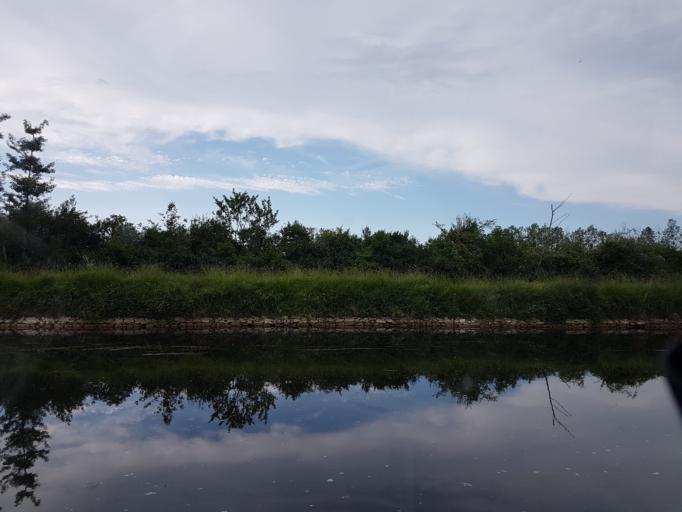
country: FR
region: Bourgogne
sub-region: Departement de l'Yonne
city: Moneteau
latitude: 47.8404
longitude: 3.5741
